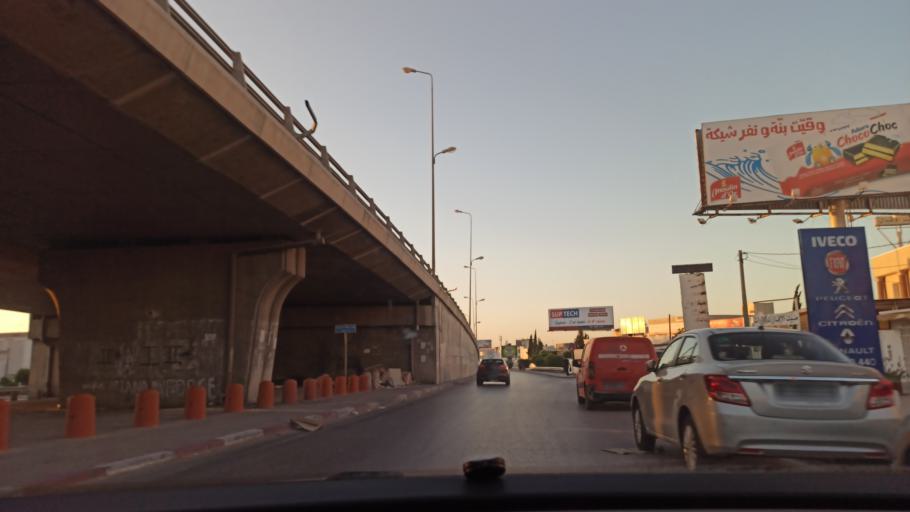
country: TN
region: Ariana
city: Ariana
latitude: 36.8596
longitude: 10.2029
